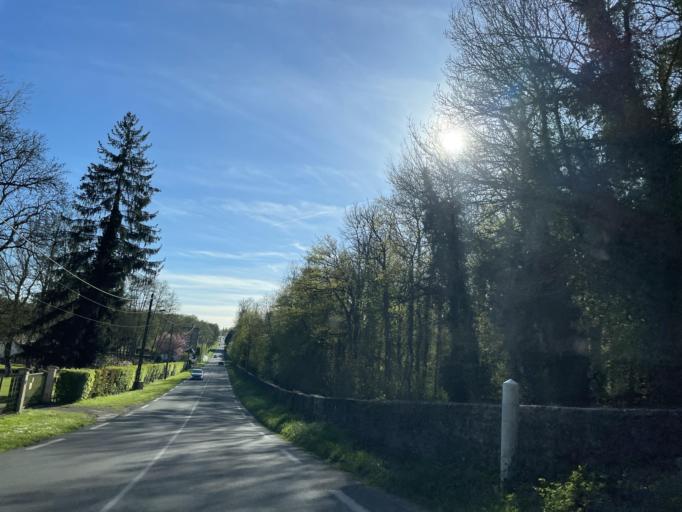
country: FR
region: Ile-de-France
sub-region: Departement de Seine-et-Marne
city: Saints
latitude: 48.7663
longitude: 3.0348
